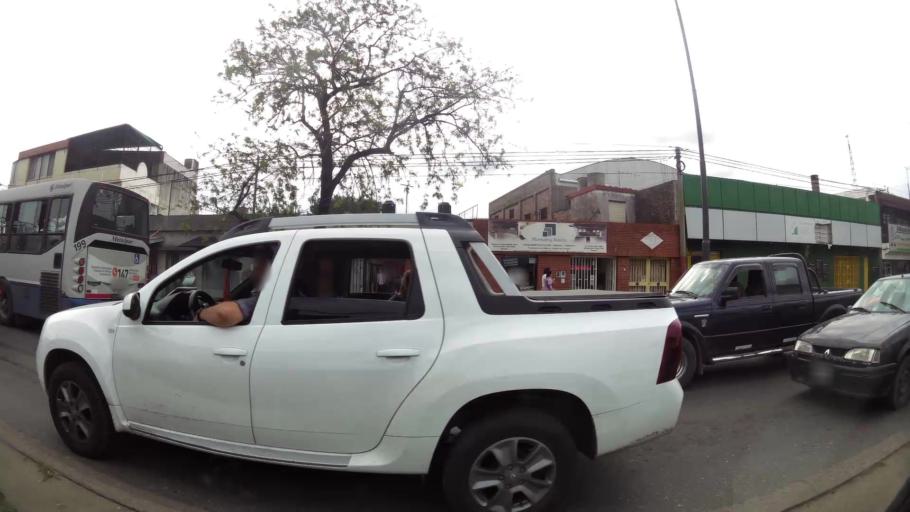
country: AR
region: Santa Fe
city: Gobernador Galvez
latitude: -33.0035
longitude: -60.6762
